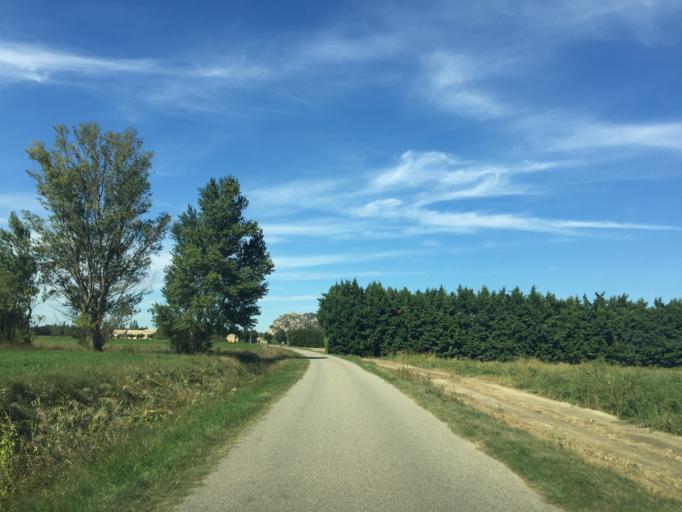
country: FR
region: Provence-Alpes-Cote d'Azur
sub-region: Departement du Vaucluse
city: Mornas
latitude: 44.1855
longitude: 4.7339
